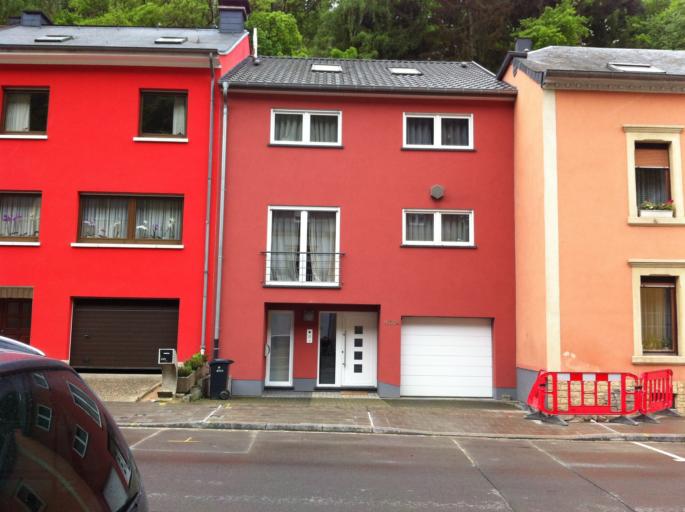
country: LU
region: Luxembourg
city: Kirchberg
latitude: 49.6239
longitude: 6.1742
